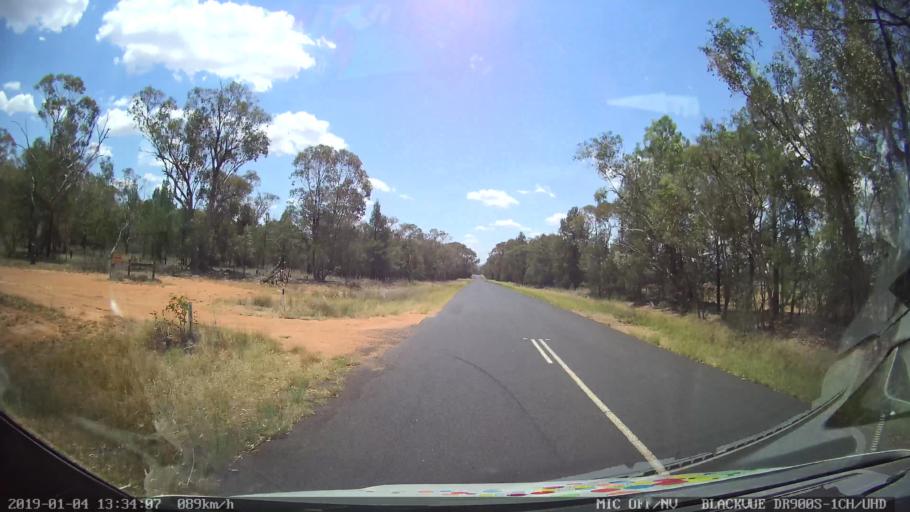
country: AU
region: New South Wales
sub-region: Dubbo Municipality
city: Dubbo
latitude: -32.5899
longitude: 148.5373
